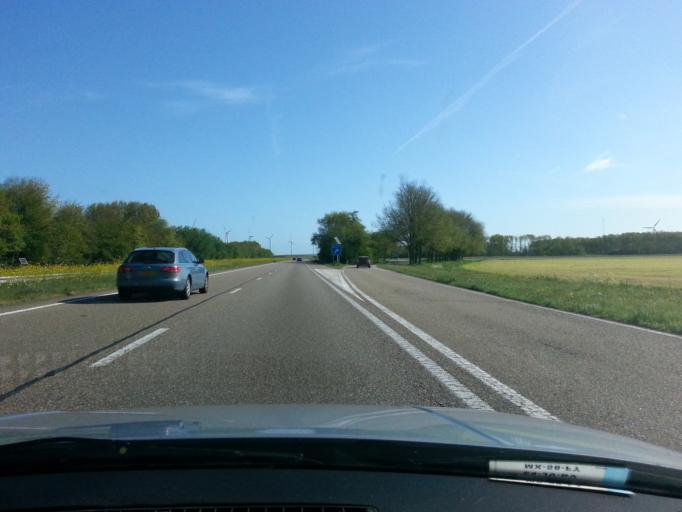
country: NL
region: Flevoland
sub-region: Gemeente Lelystad
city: Lelystad
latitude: 52.5780
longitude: 5.5427
